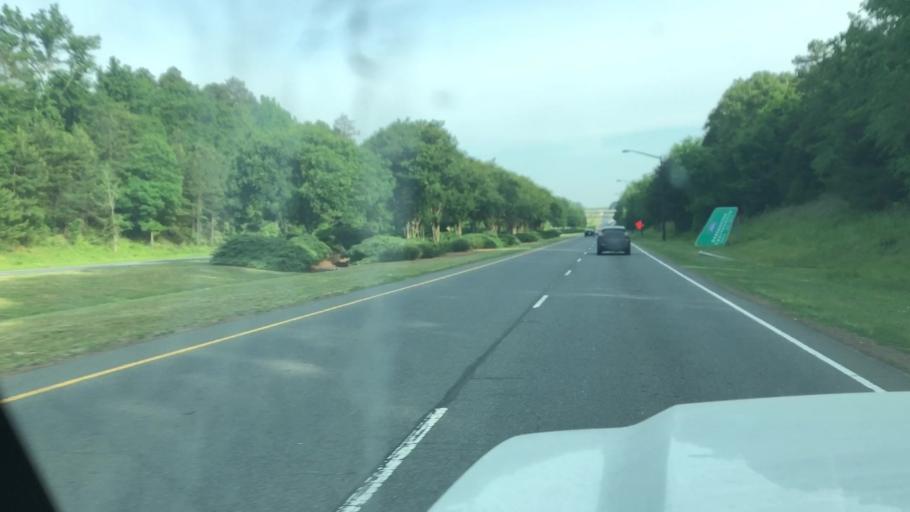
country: US
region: North Carolina
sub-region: Gaston County
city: Mount Holly
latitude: 35.3151
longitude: -80.9321
